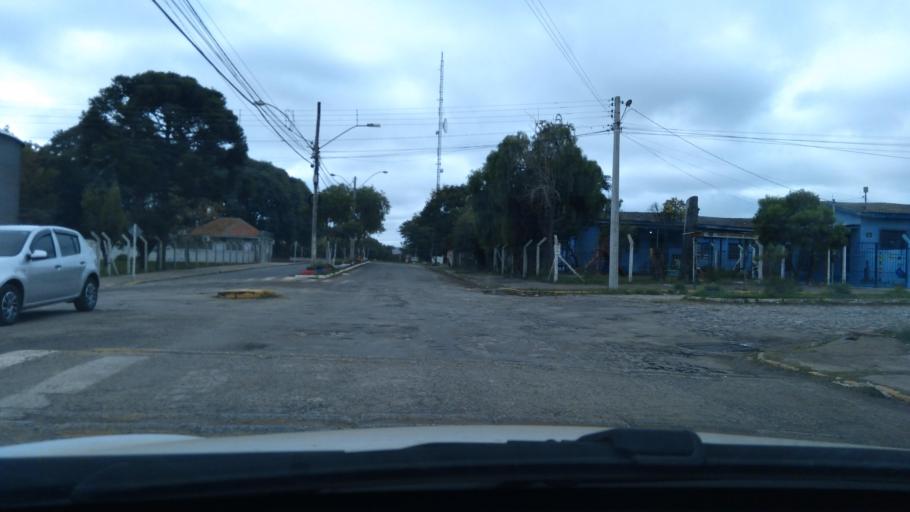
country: BR
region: Rio Grande do Sul
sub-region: Dom Pedrito
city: Dom Pedrito
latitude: -30.9688
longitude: -54.6727
